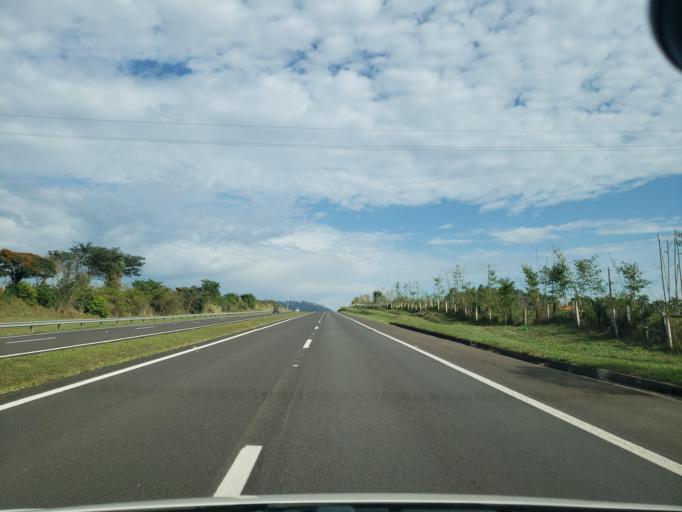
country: BR
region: Sao Paulo
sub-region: Dois Corregos
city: Dois Corregos
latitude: -22.2439
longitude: -48.3147
